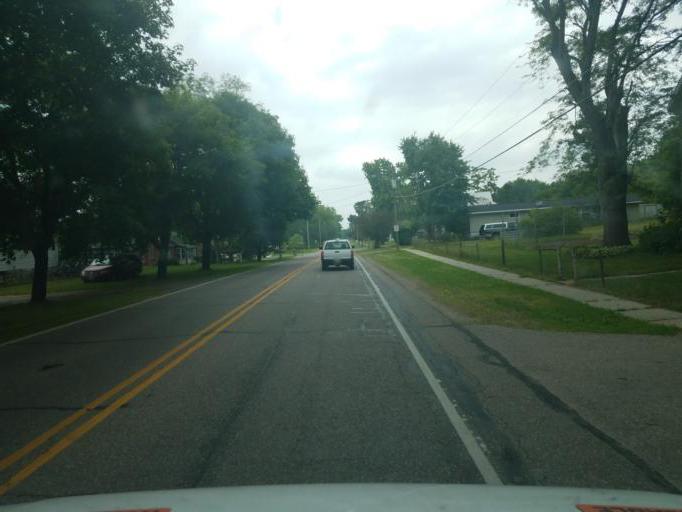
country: US
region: Wisconsin
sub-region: Juneau County
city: Elroy
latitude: 43.6432
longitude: -90.2178
